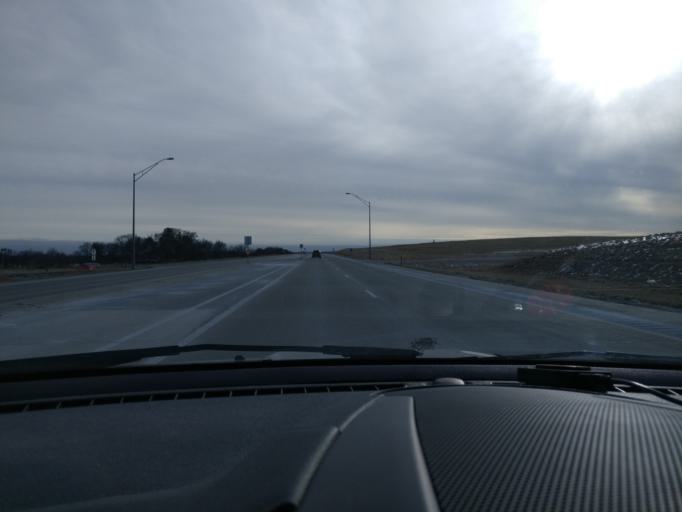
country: US
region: Nebraska
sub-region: Saunders County
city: Wahoo
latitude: 41.2205
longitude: -96.6374
